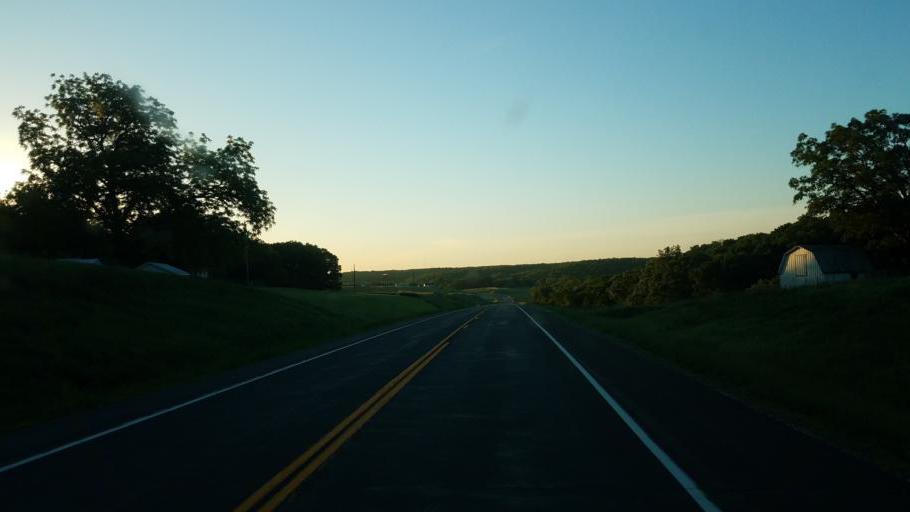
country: US
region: Missouri
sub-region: Schuyler County
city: Lancaster
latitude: 40.4881
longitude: -92.6421
